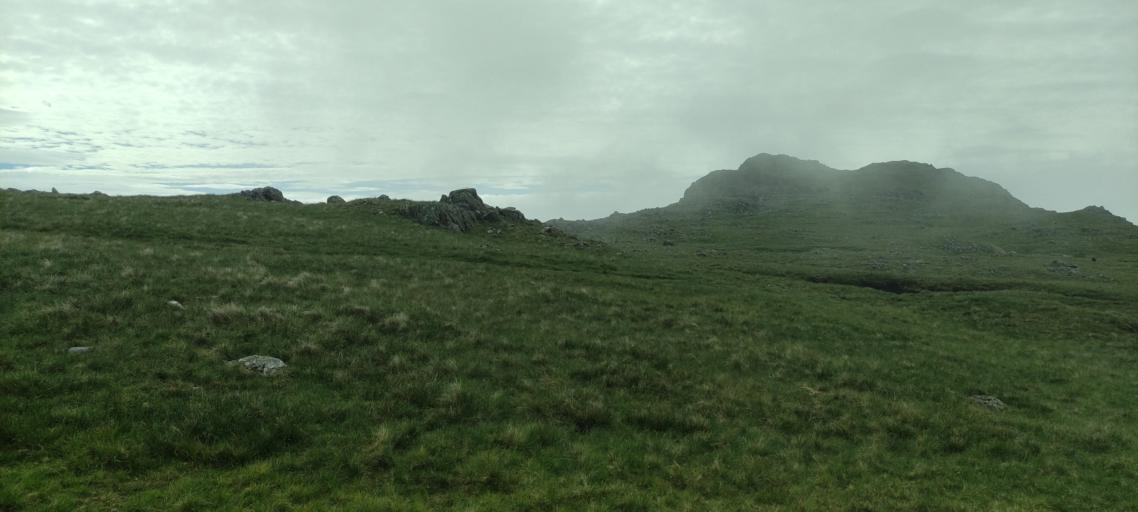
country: GB
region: England
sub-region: Cumbria
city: Keswick
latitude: 54.4599
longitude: -3.1134
